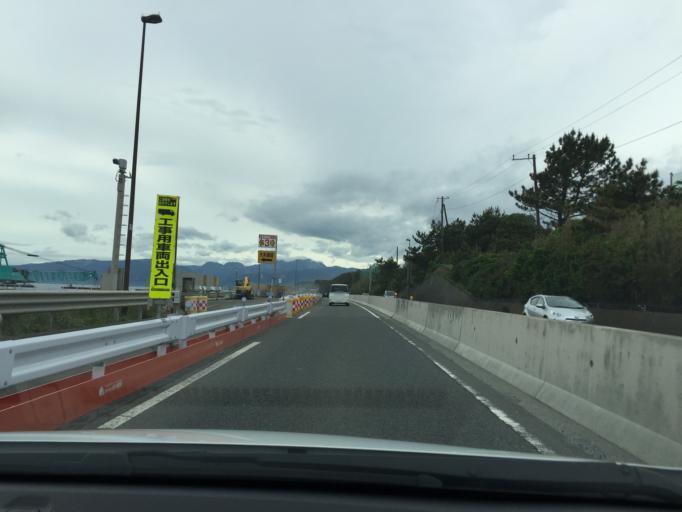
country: JP
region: Kanagawa
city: Ninomiya
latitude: 35.2990
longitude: 139.2742
